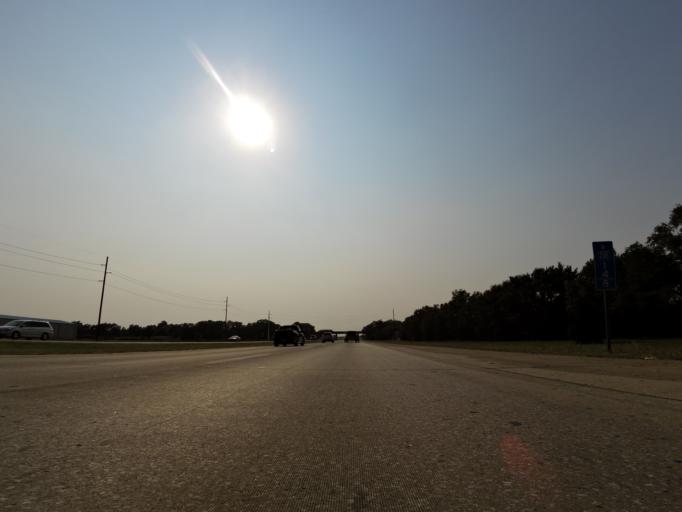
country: US
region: Kansas
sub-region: Sedgwick County
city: Park City
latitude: 37.7568
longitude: -97.3501
